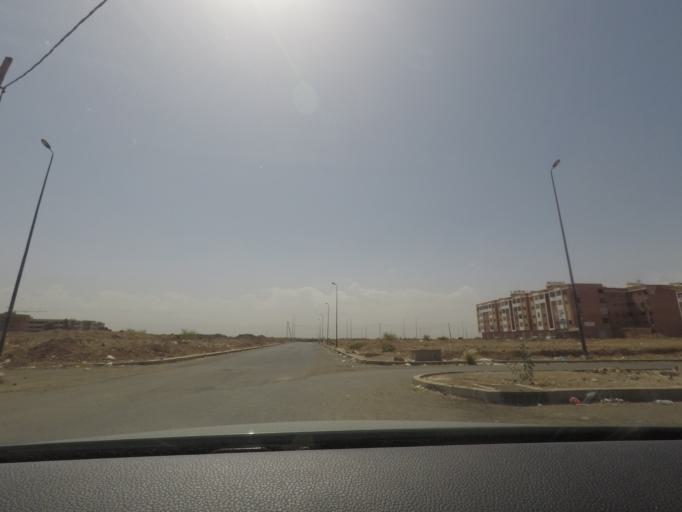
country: MA
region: Marrakech-Tensift-Al Haouz
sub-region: Marrakech
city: Marrakesh
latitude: 31.5850
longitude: -8.0382
